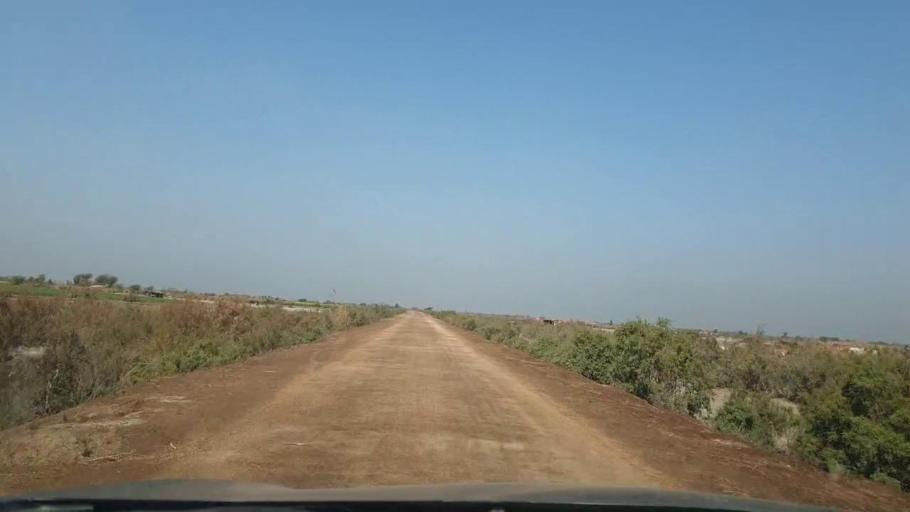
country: PK
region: Sindh
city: Berani
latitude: 25.7024
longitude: 68.8679
